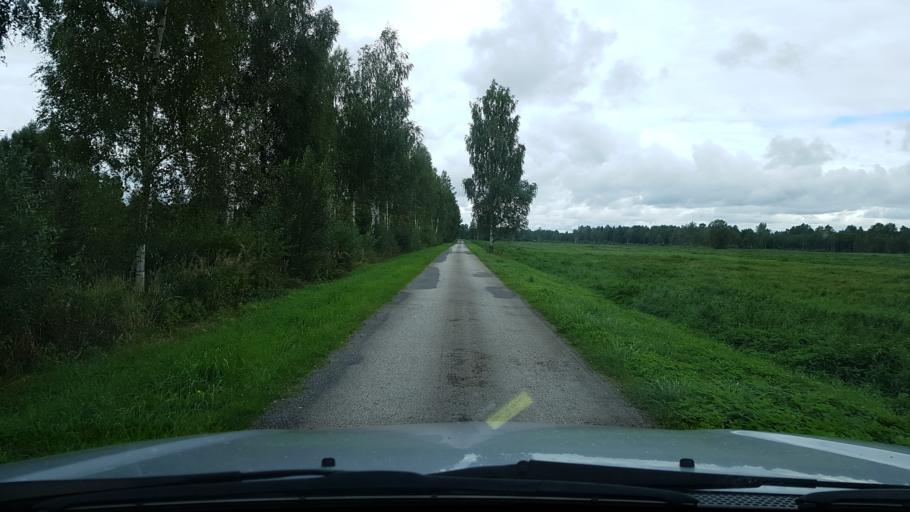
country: EE
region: Harju
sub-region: Raasiku vald
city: Arukula
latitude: 59.2969
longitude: 25.0567
